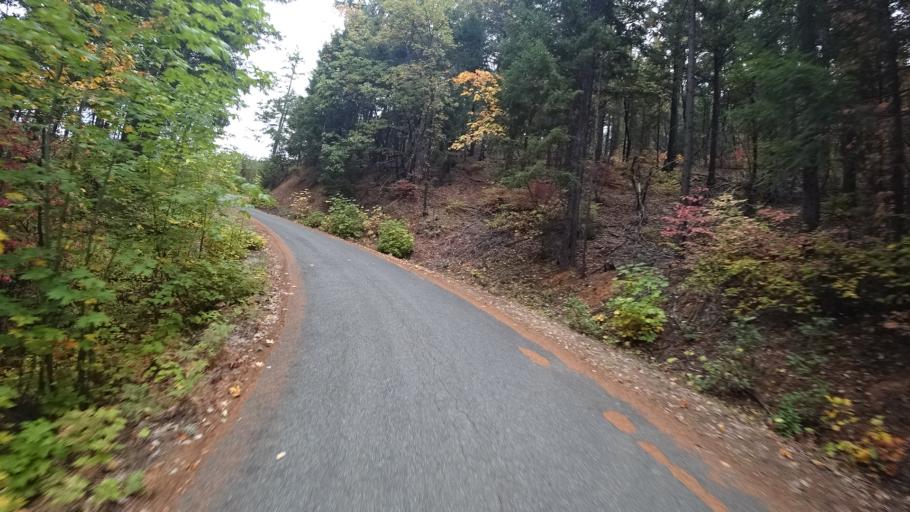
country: US
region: California
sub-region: Siskiyou County
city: Happy Camp
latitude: 41.8235
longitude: -123.3299
